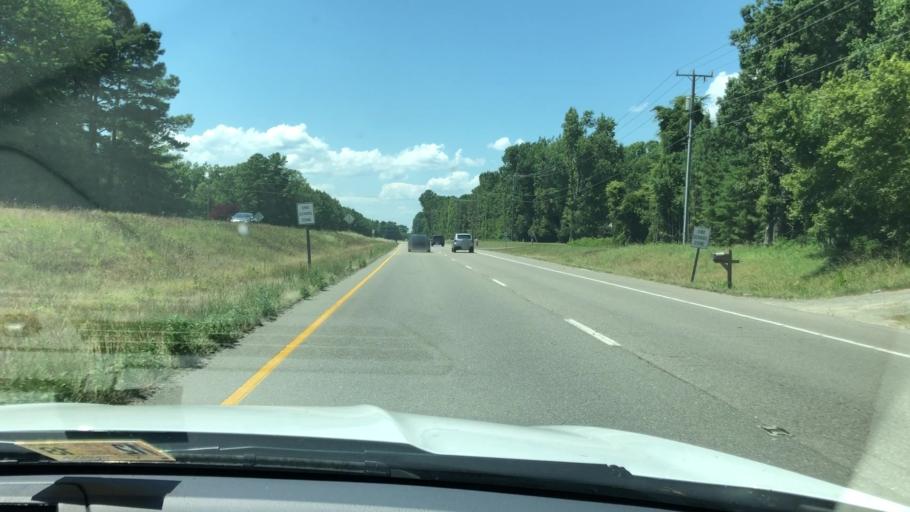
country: US
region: Virginia
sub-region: Middlesex County
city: Saluda
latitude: 37.5939
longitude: -76.5008
